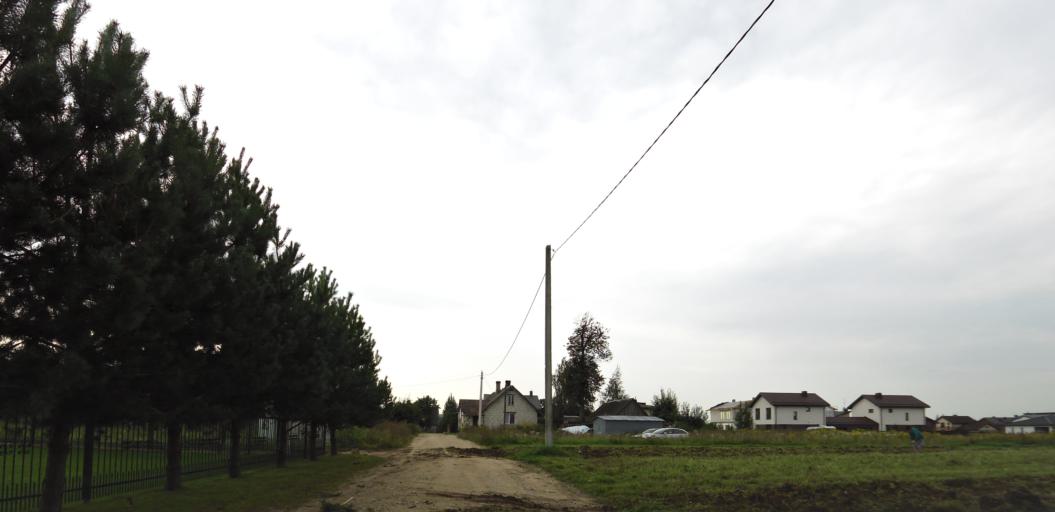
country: LT
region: Vilnius County
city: Pasilaiciai
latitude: 54.7603
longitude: 25.2300
